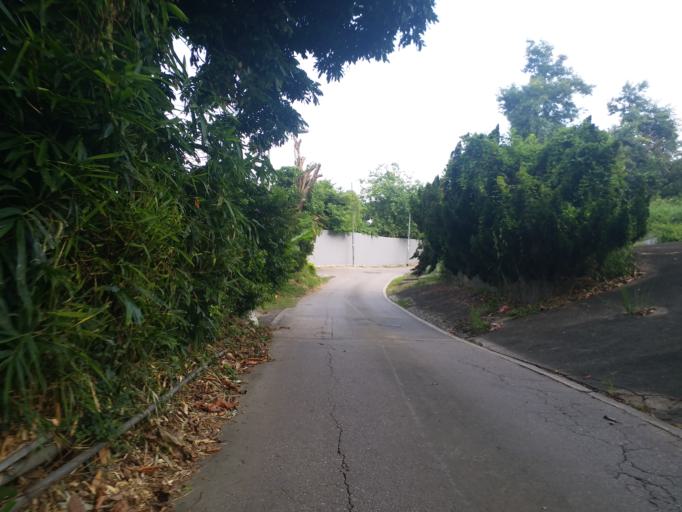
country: HK
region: Yuen Long
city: Yuen Long Kau Hui
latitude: 22.4456
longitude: 114.0111
